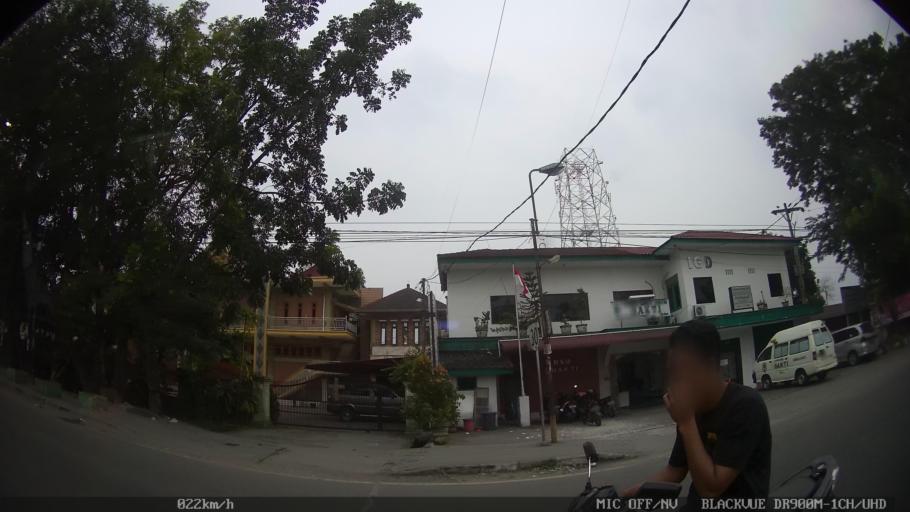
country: ID
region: North Sumatra
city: Medan
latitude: 3.5686
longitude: 98.7011
